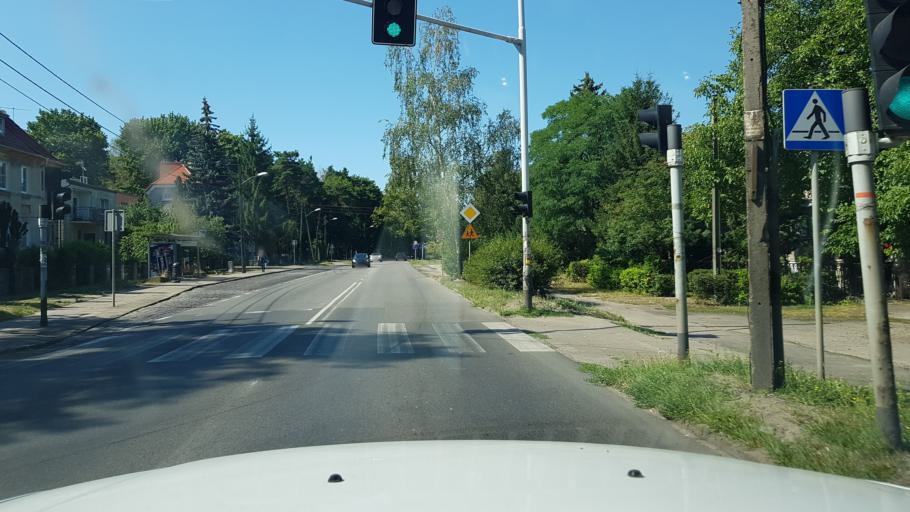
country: PL
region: West Pomeranian Voivodeship
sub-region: Szczecin
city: Szczecin
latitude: 53.4015
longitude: 14.6871
